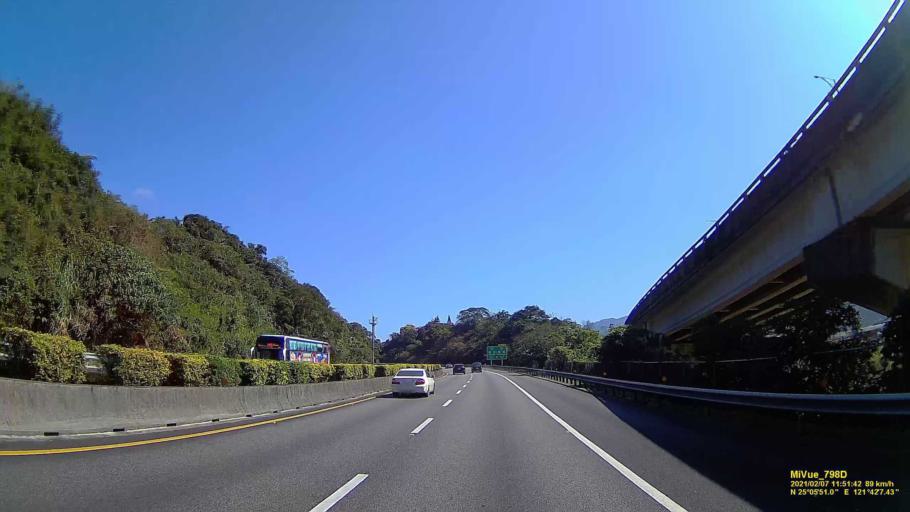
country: TW
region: Taiwan
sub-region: Keelung
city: Keelung
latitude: 25.0974
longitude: 121.7022
